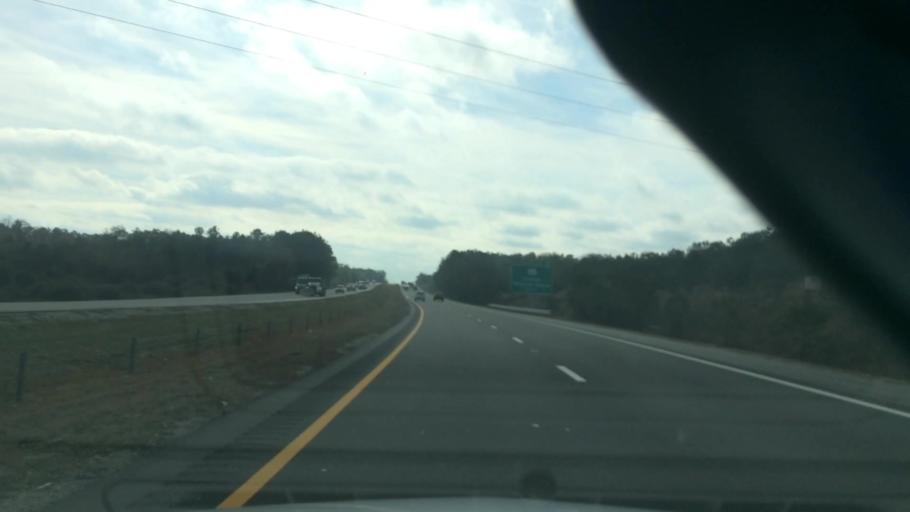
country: US
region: North Carolina
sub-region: New Hanover County
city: Wrightsboro
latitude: 34.3140
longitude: -77.9464
